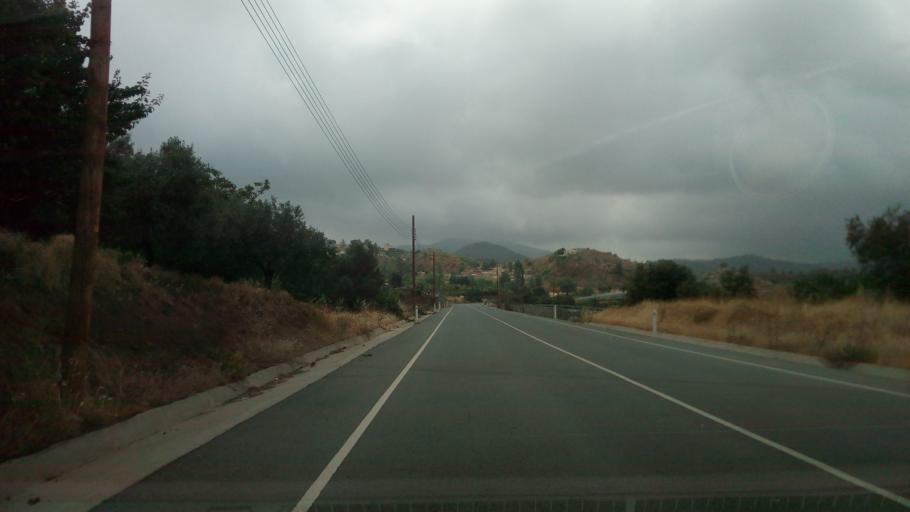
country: CY
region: Limassol
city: Pelendri
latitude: 34.8538
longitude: 33.0095
